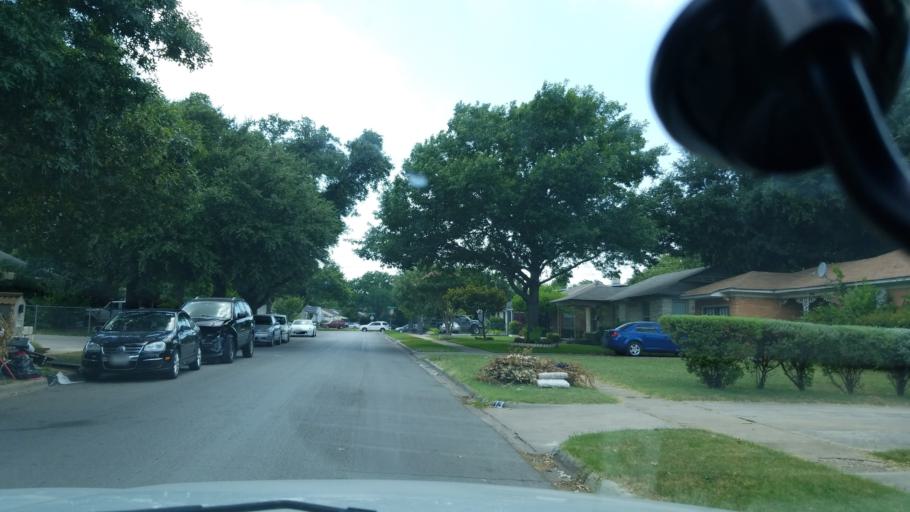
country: US
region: Texas
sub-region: Dallas County
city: Cockrell Hill
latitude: 32.7236
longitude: -96.8732
